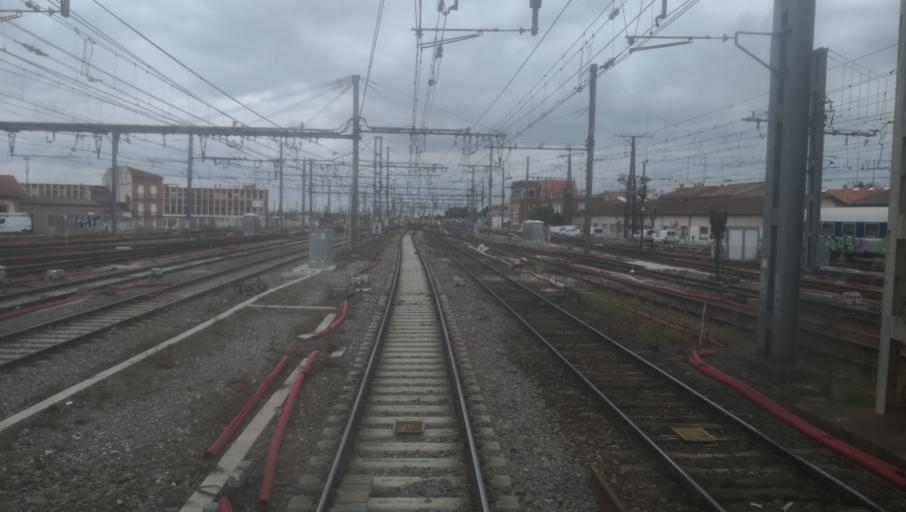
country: FR
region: Midi-Pyrenees
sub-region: Departement de la Haute-Garonne
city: Toulouse
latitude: 43.6144
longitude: 1.4534
